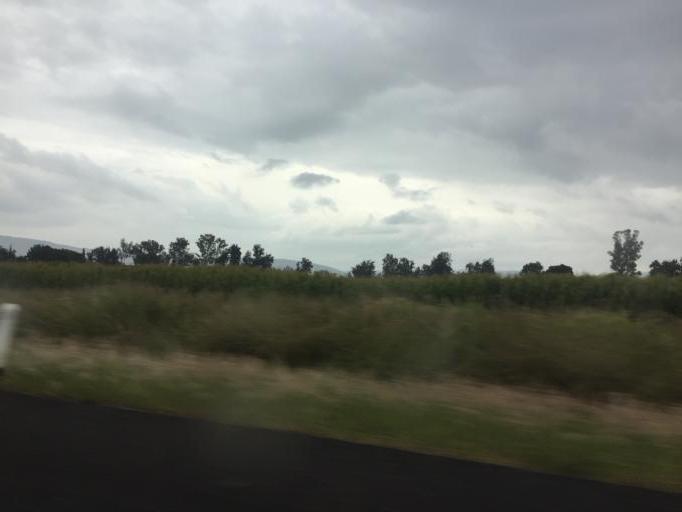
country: MX
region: Jalisco
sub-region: Zapotlan del Rey
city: Zapotlan del Rey
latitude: 20.4553
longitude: -102.8918
